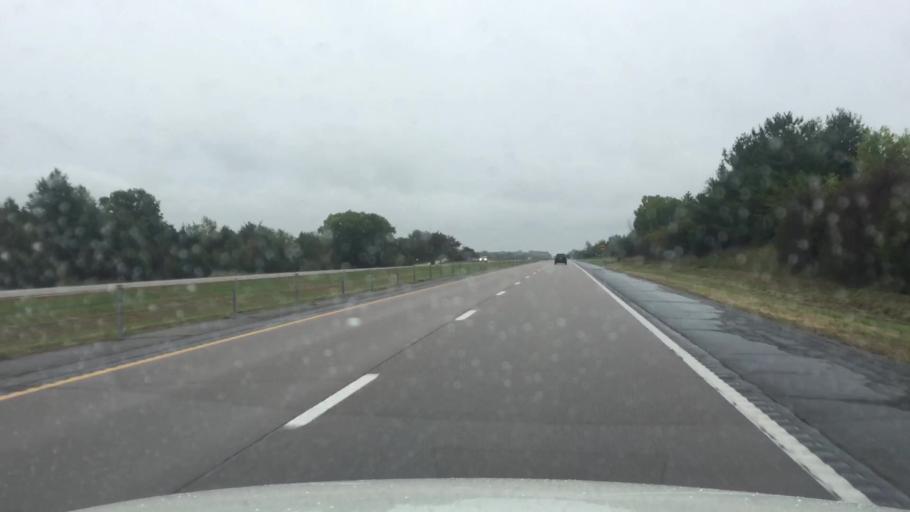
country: US
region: Missouri
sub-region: Boone County
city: Ashland
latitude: 38.7190
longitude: -92.2545
